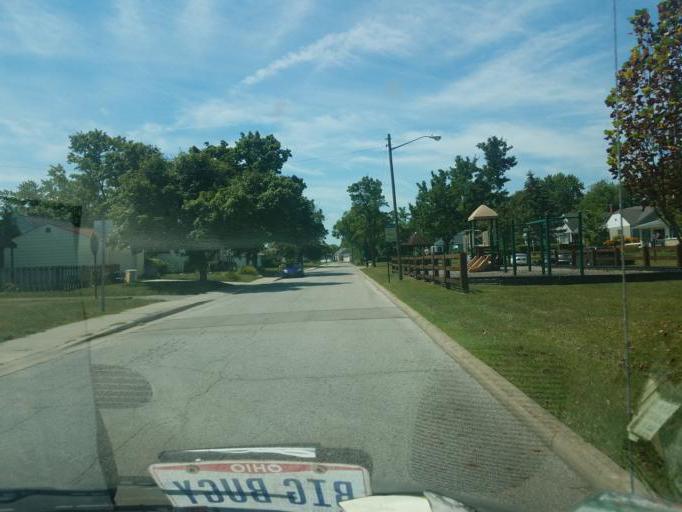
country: US
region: Ohio
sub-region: Franklin County
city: Grove City
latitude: 39.8793
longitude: -83.0940
